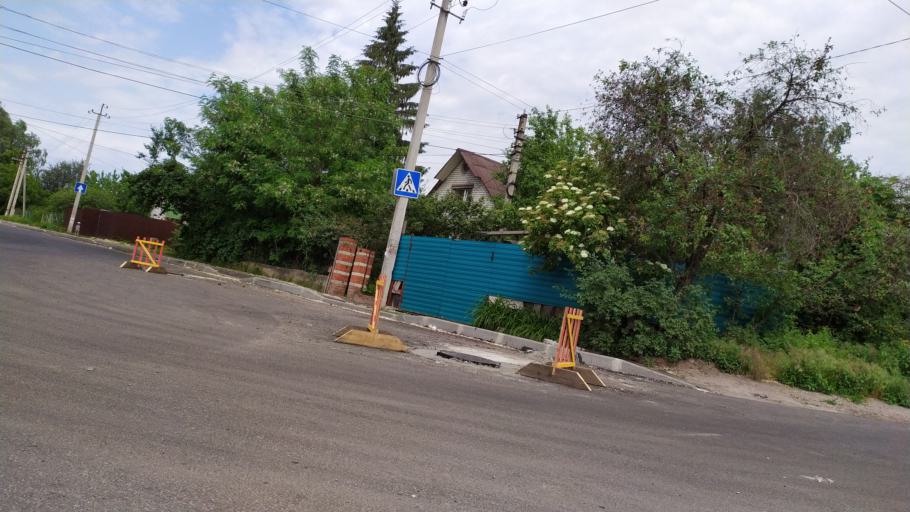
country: RU
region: Kursk
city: Kursk
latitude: 51.6646
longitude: 36.1508
